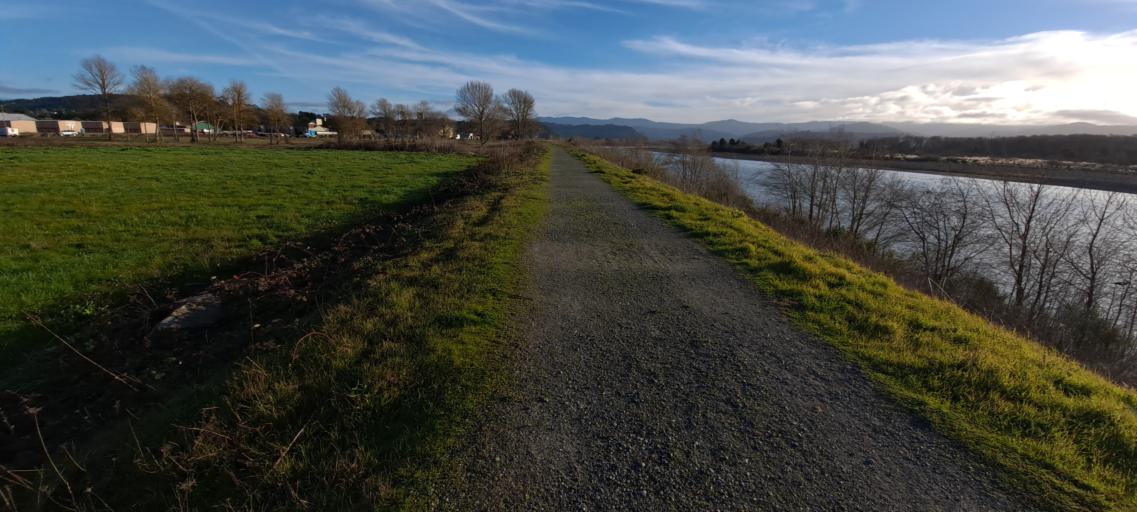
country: US
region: California
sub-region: Humboldt County
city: Fortuna
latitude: 40.5814
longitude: -124.1566
